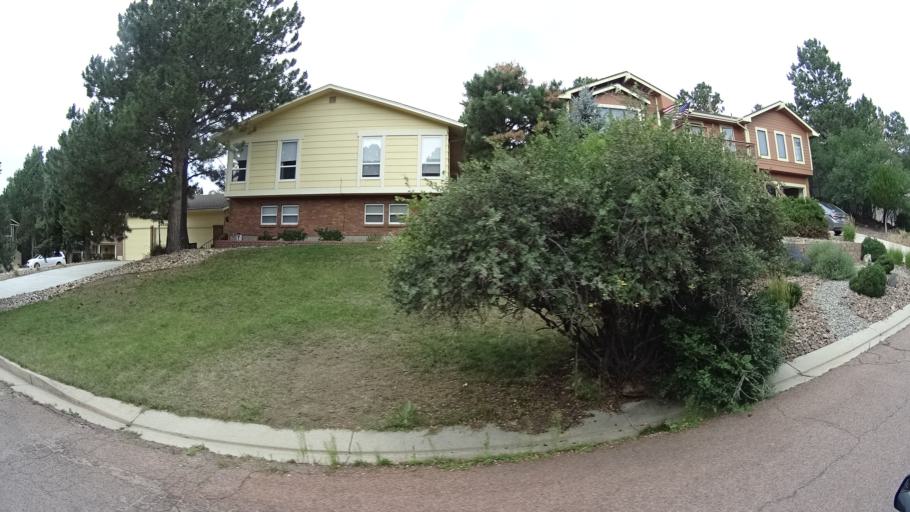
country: US
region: Colorado
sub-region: El Paso County
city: Air Force Academy
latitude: 38.9317
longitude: -104.8396
